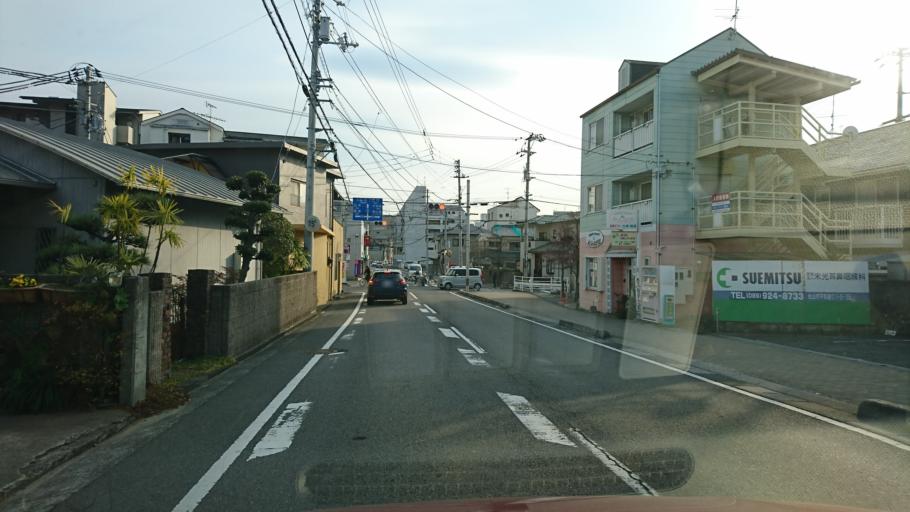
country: JP
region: Ehime
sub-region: Shikoku-chuo Shi
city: Matsuyama
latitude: 33.8539
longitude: 132.7762
